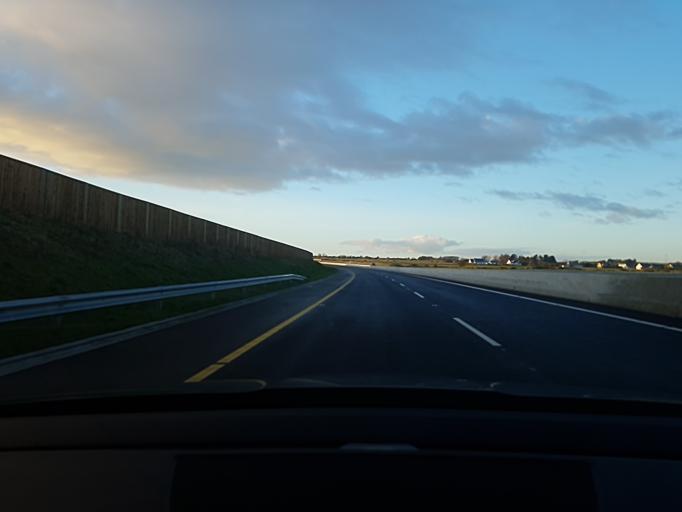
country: IE
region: Connaught
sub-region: County Galway
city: Athenry
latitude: 53.3929
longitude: -8.8036
